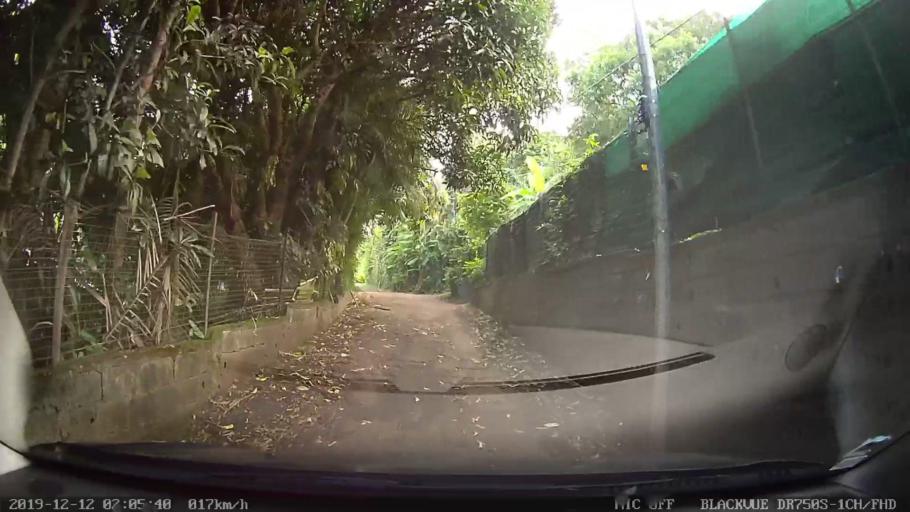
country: RE
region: Reunion
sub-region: Reunion
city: Sainte-Marie
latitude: -20.9340
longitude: 55.5282
